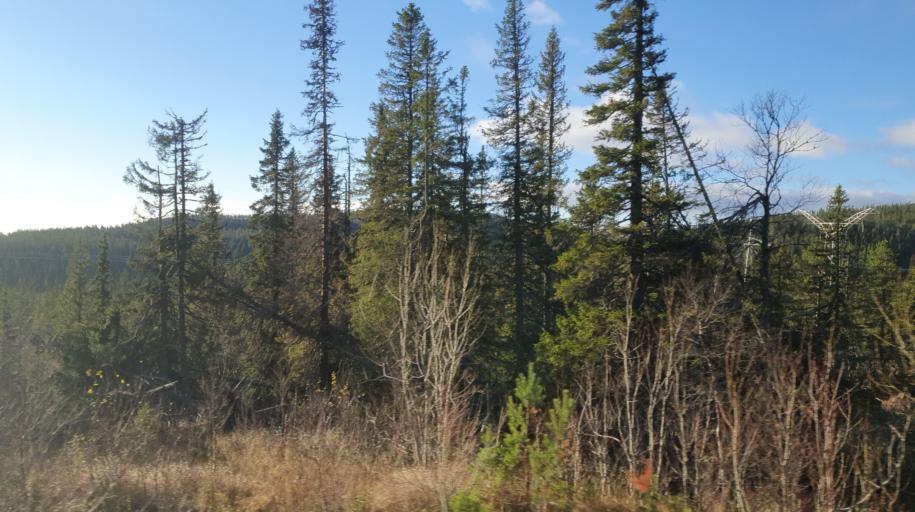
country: NO
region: Buskerud
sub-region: Krodsherad
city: Noresund
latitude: 60.2186
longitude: 9.5350
